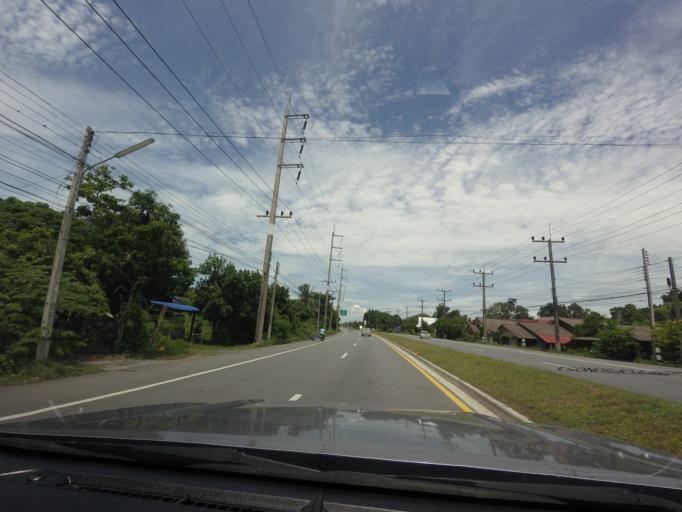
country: TH
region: Songkhla
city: Krasae Sin
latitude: 7.5890
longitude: 100.4047
